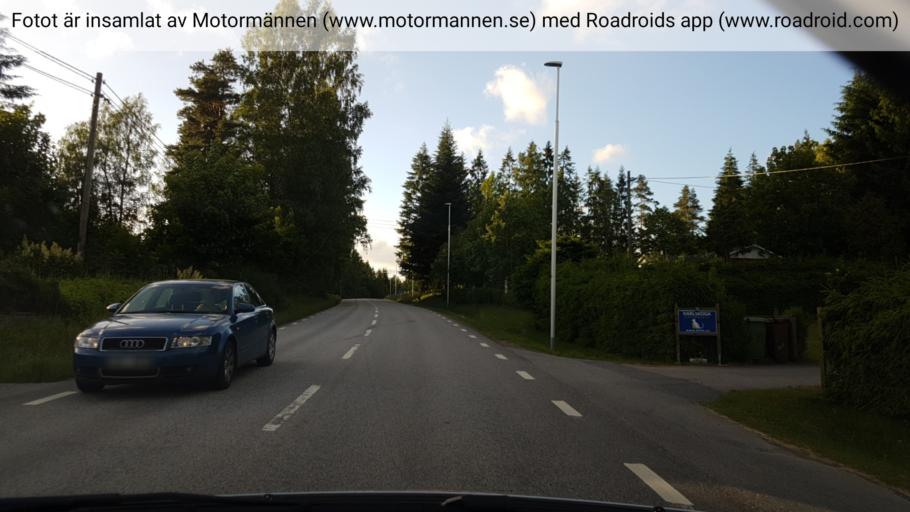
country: SE
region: OErebro
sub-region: Karlskoga Kommun
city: Karlskoga
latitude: 59.3581
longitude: 14.5727
